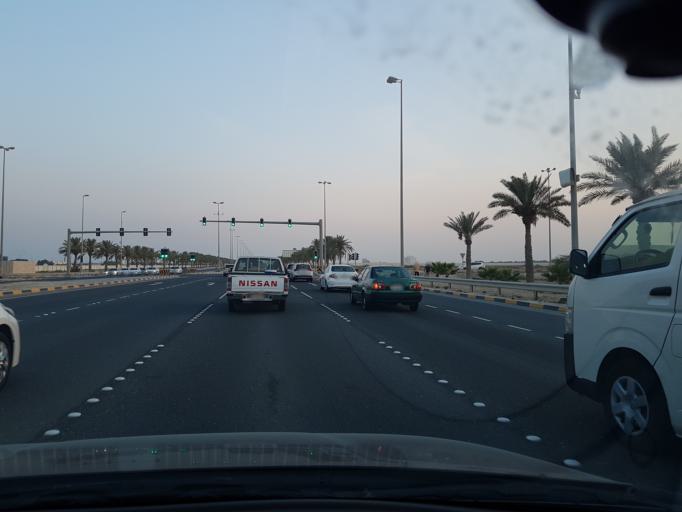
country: BH
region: Central Governorate
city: Dar Kulayb
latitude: 26.0486
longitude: 50.4998
